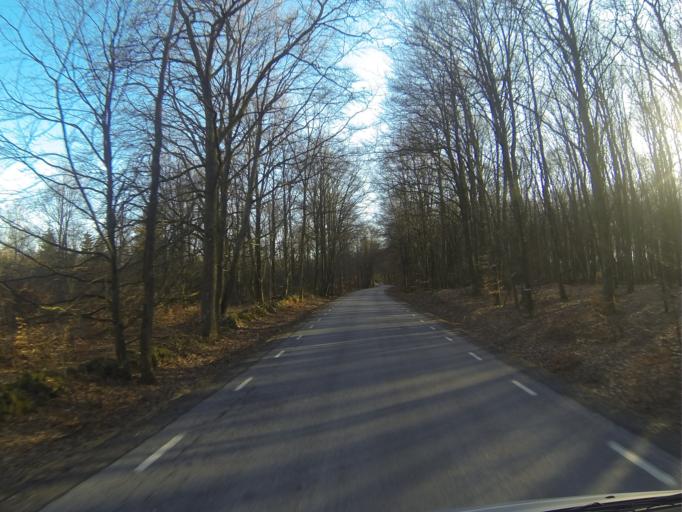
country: SE
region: Skane
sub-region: Horby Kommun
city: Hoerby
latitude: 55.9165
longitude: 13.6663
